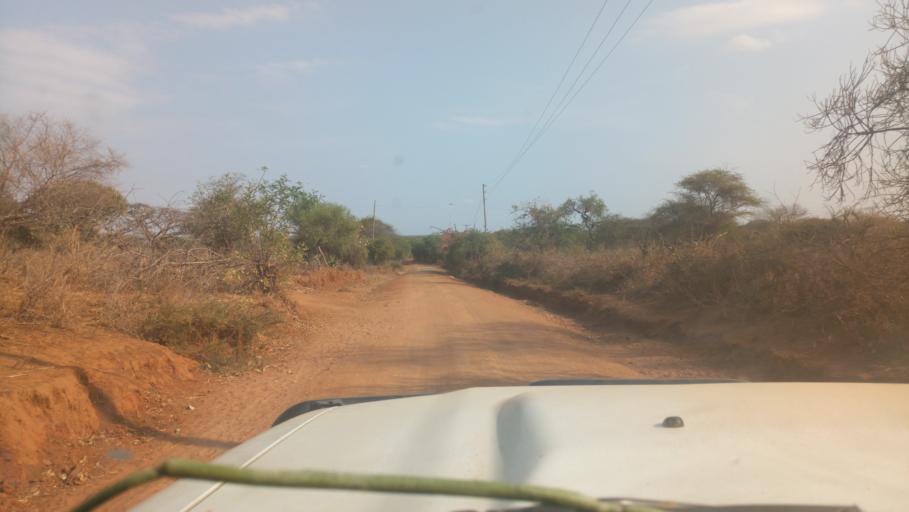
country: KE
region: Kitui
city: Kitui
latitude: -1.6629
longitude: 37.9237
